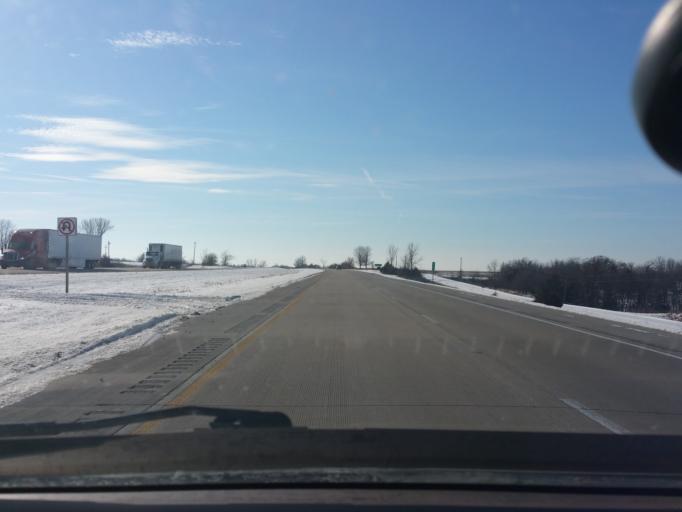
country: US
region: Iowa
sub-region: Decatur County
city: Leon
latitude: 40.7997
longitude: -93.8329
